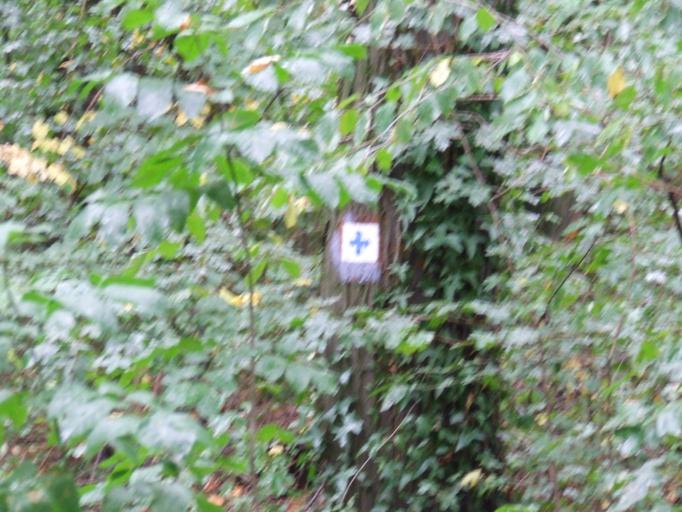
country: HU
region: Somogy
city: Kaposvar
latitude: 46.3269
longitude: 17.7910
